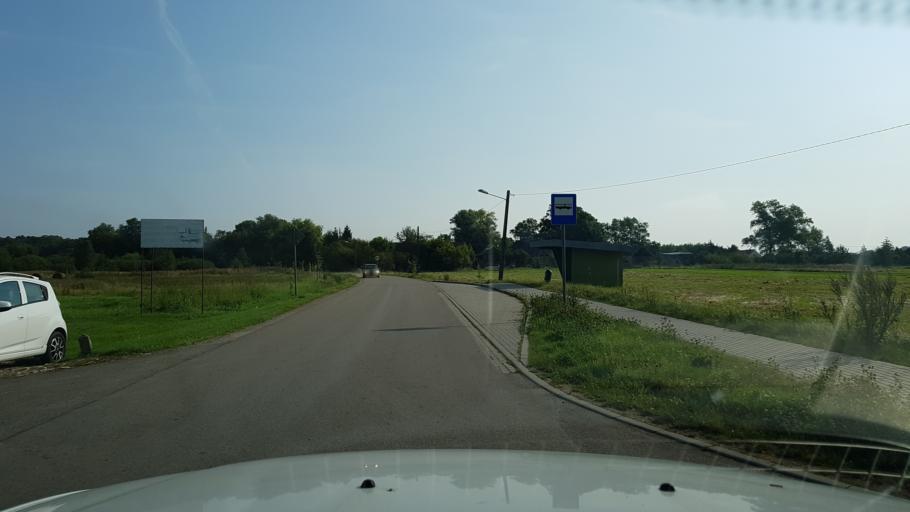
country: PL
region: West Pomeranian Voivodeship
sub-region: Powiat slawienski
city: Slawno
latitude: 54.3699
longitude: 16.5754
